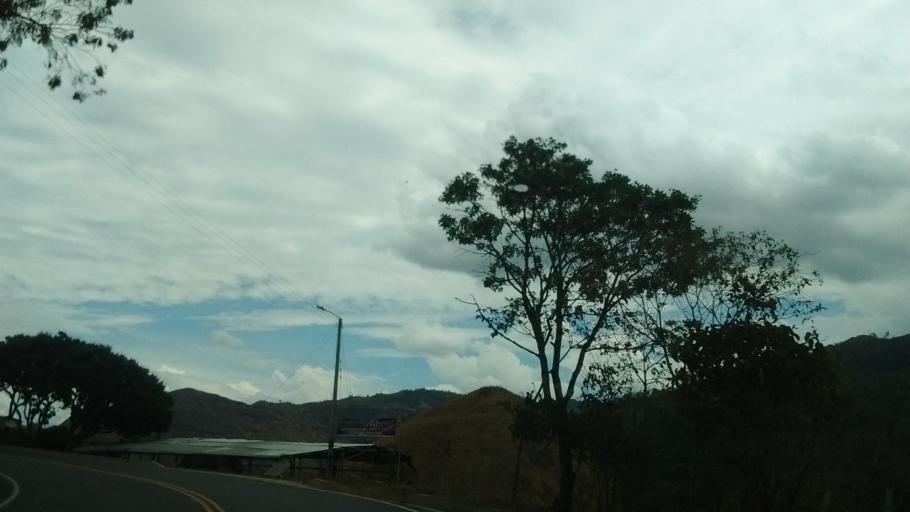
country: CO
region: Cauca
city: Rosas
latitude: 2.2793
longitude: -76.7105
